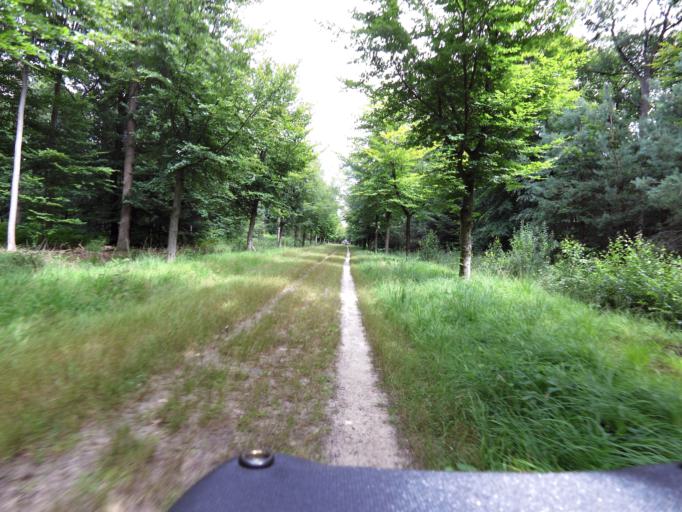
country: NL
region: North Brabant
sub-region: Gemeente Breda
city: Breda
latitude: 51.5827
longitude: 4.7057
